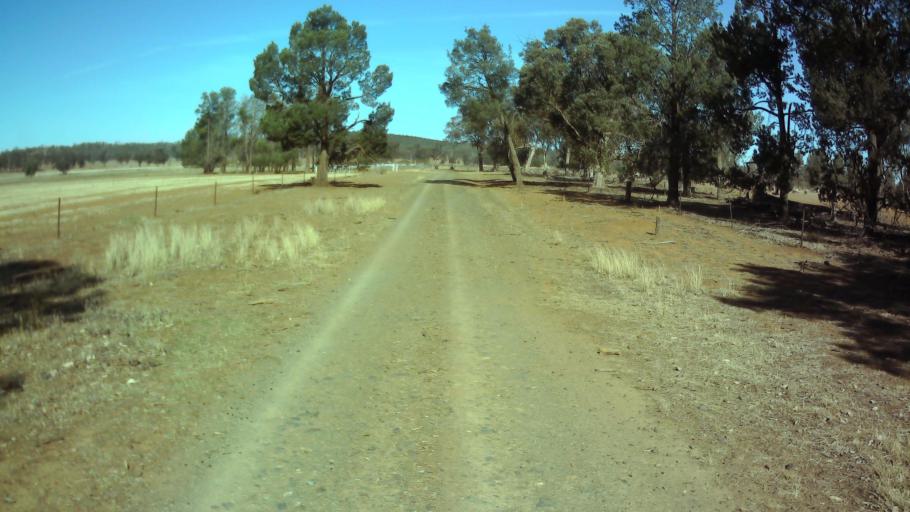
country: AU
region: New South Wales
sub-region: Weddin
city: Grenfell
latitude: -33.7804
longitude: 147.8378
